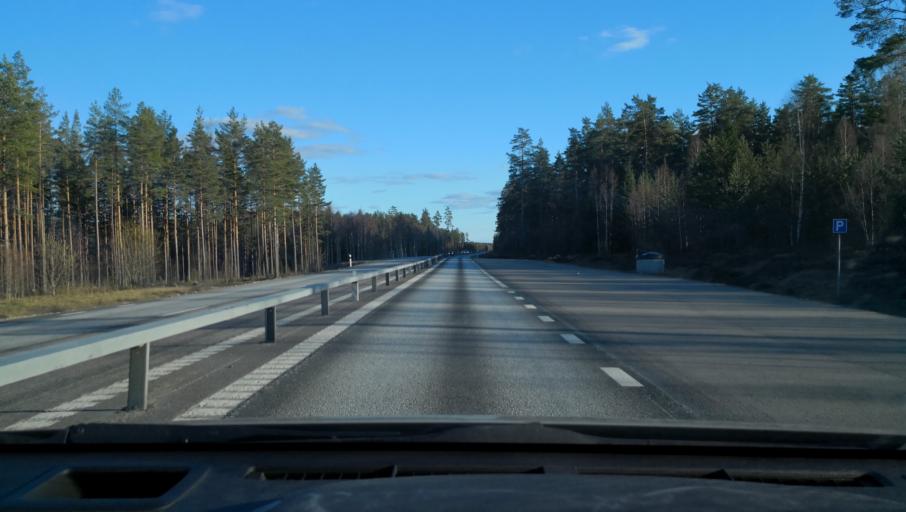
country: SE
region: Dalarna
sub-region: Avesta Kommun
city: Avesta
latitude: 60.0570
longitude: 16.3364
